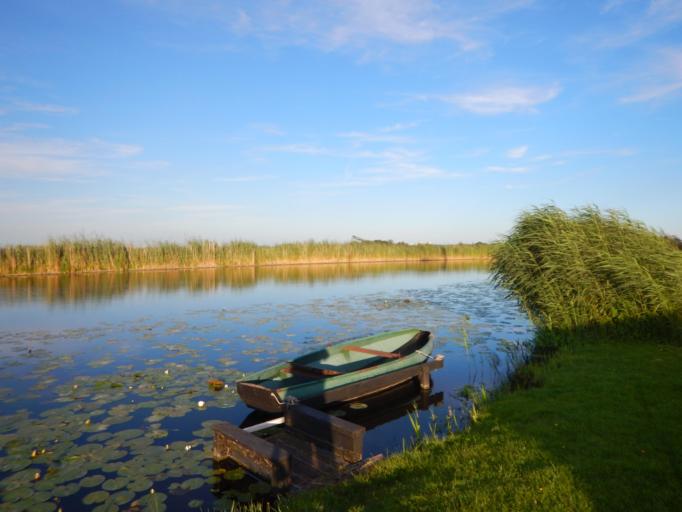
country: NL
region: South Holland
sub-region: Gemeente Voorschoten
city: Voorschoten
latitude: 52.0788
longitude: 4.4205
